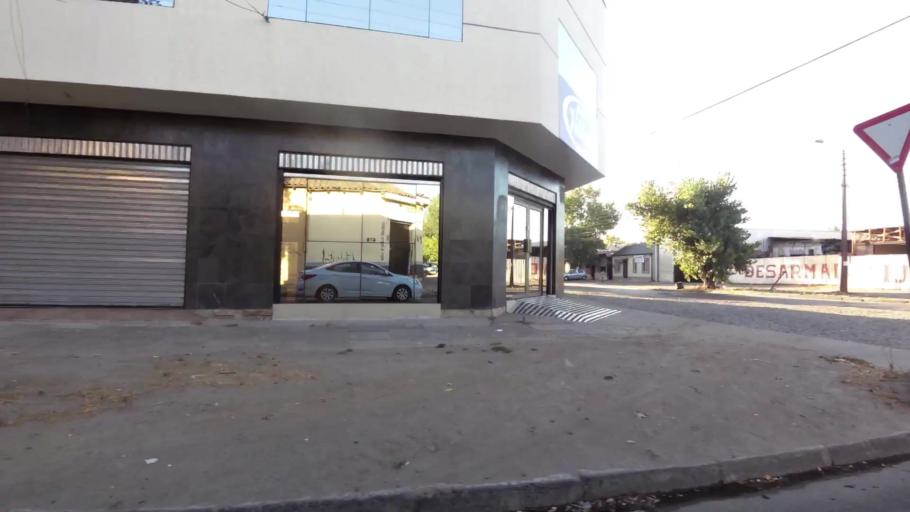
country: CL
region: Maule
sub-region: Provincia de Talca
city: Talca
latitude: -35.4339
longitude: -71.6470
